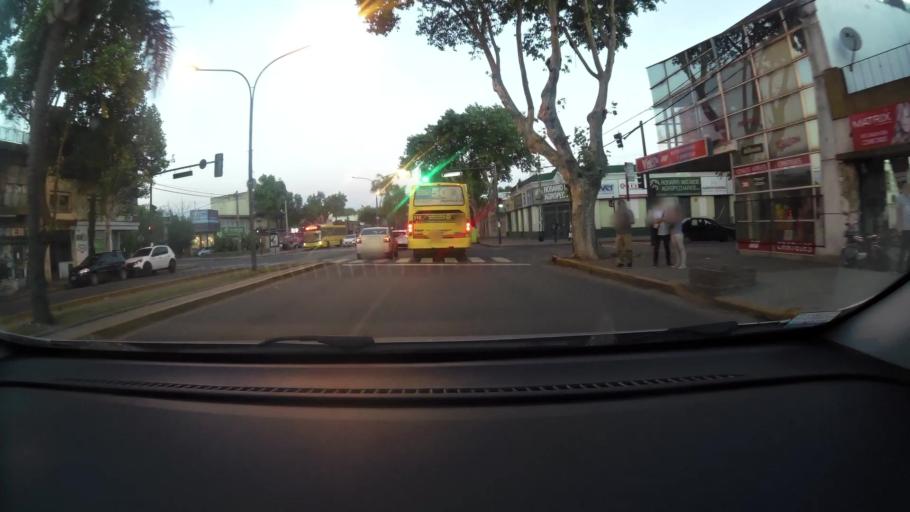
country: AR
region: Santa Fe
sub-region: Departamento de Rosario
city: Rosario
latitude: -32.9571
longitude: -60.6781
